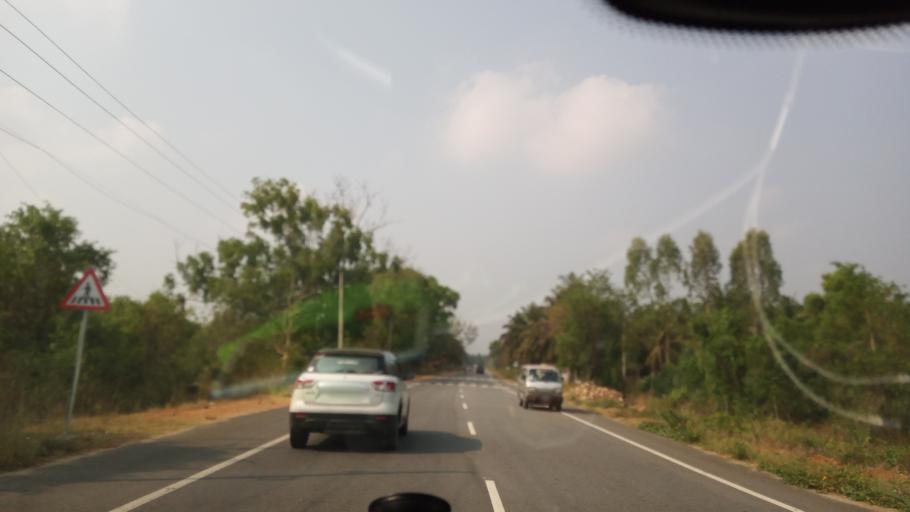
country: IN
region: Karnataka
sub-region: Mandya
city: Nagamangala
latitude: 12.7750
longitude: 76.7411
